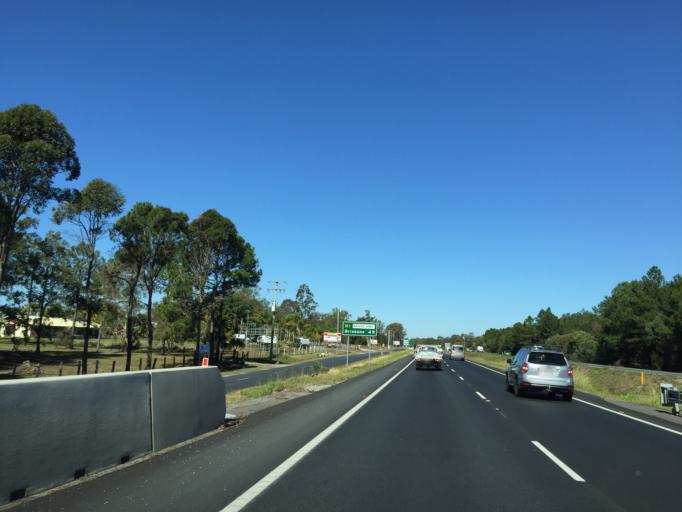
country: AU
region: Queensland
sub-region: Moreton Bay
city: Caboolture
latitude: -27.0484
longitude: 152.9774
